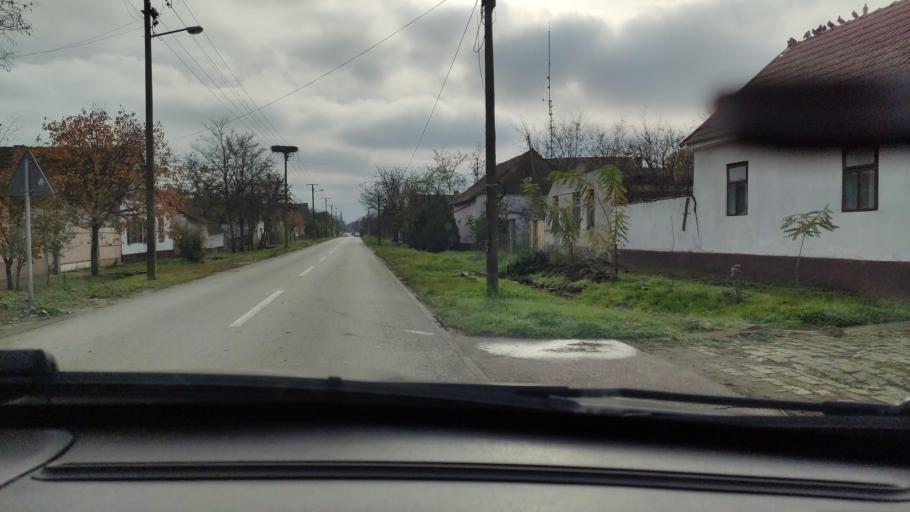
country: RS
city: Jazovo
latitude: 45.9033
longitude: 20.2164
